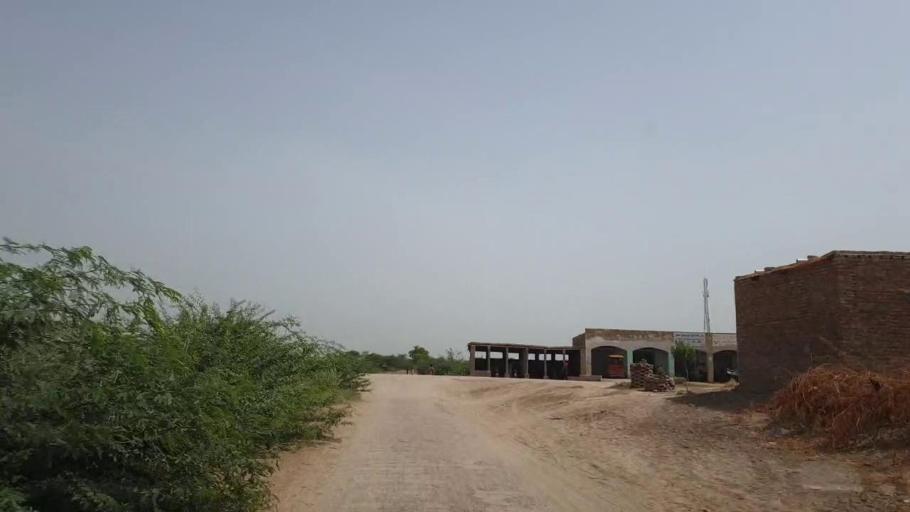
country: PK
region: Sindh
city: Sakrand
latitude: 26.1409
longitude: 68.3642
